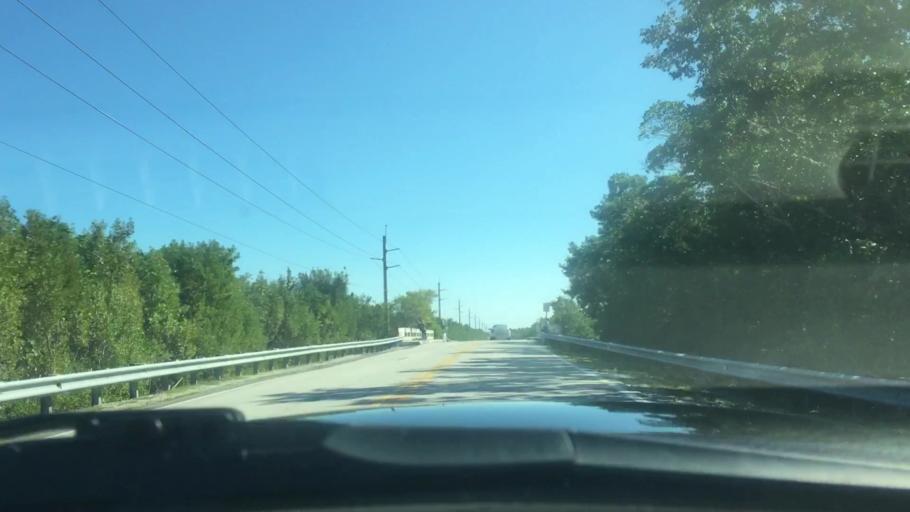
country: US
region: Florida
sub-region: Monroe County
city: North Key Largo
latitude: 25.2828
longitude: -80.3549
